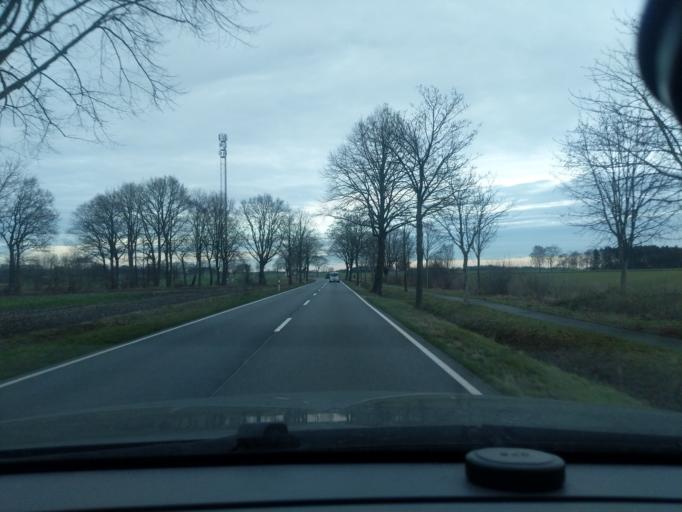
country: DE
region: Lower Saxony
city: Sauensiek
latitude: 53.3951
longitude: 9.6083
